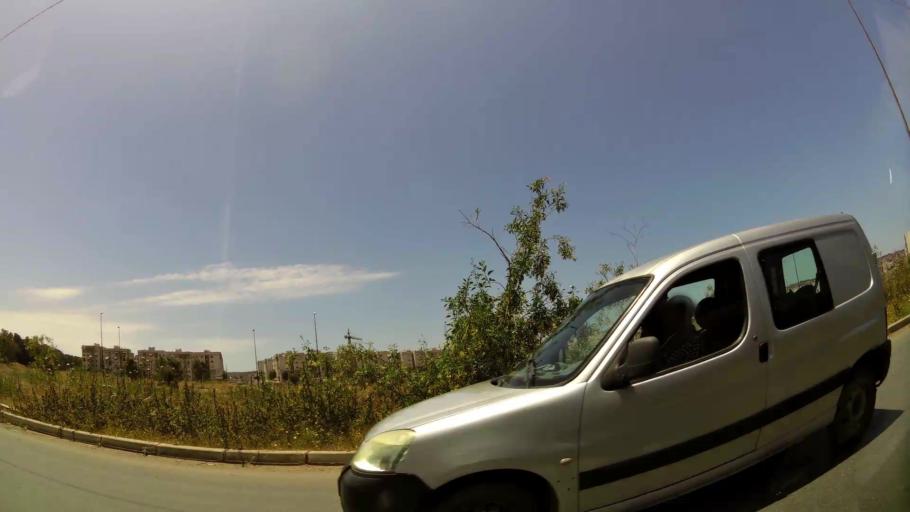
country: MA
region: Gharb-Chrarda-Beni Hssen
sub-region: Kenitra Province
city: Kenitra
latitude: 34.2522
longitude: -6.6335
